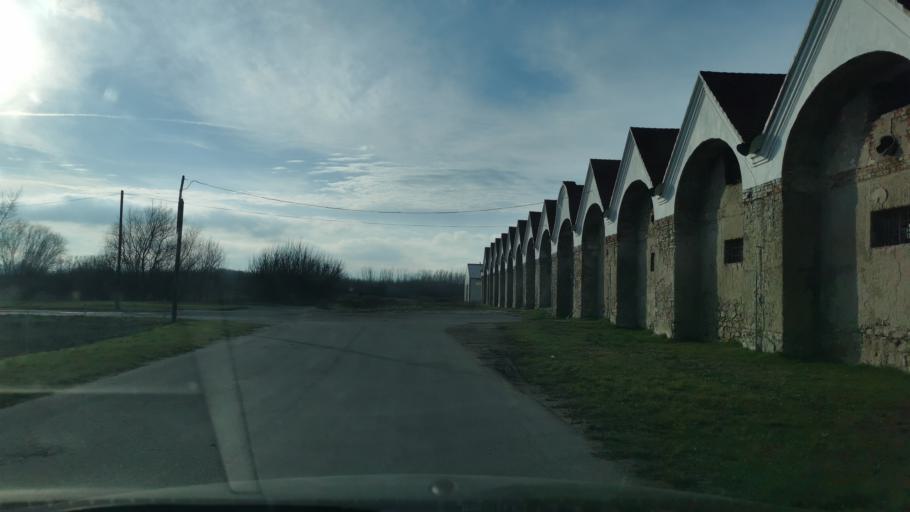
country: CZ
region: South Moravian
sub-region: Okres Hodonin
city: Mikulcice
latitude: 48.7820
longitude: 17.1045
